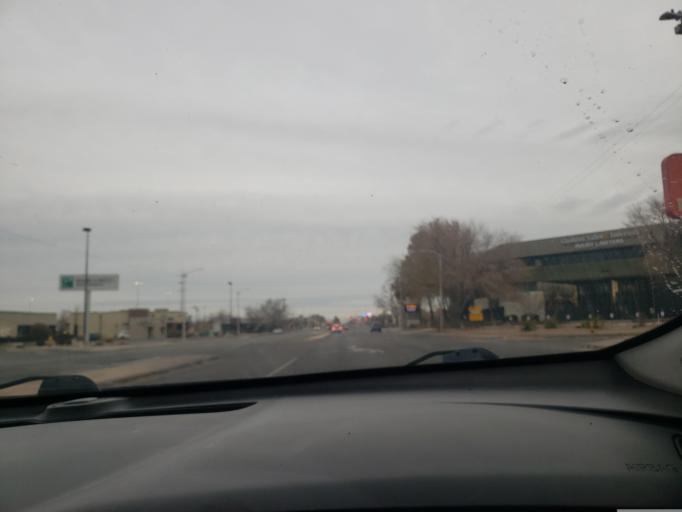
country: US
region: New Mexico
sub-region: Bernalillo County
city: North Valley
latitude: 35.1287
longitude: -106.5864
